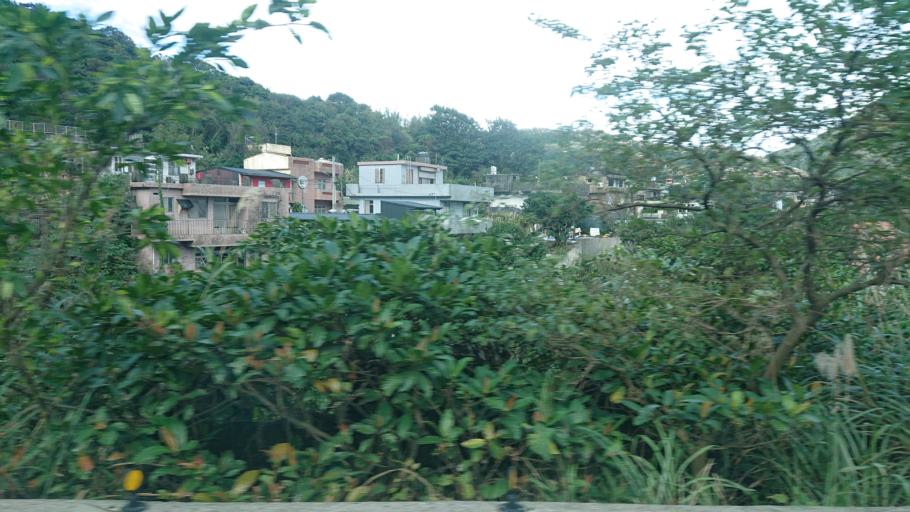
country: TW
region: Taiwan
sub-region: Keelung
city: Keelung
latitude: 25.1071
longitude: 121.8523
